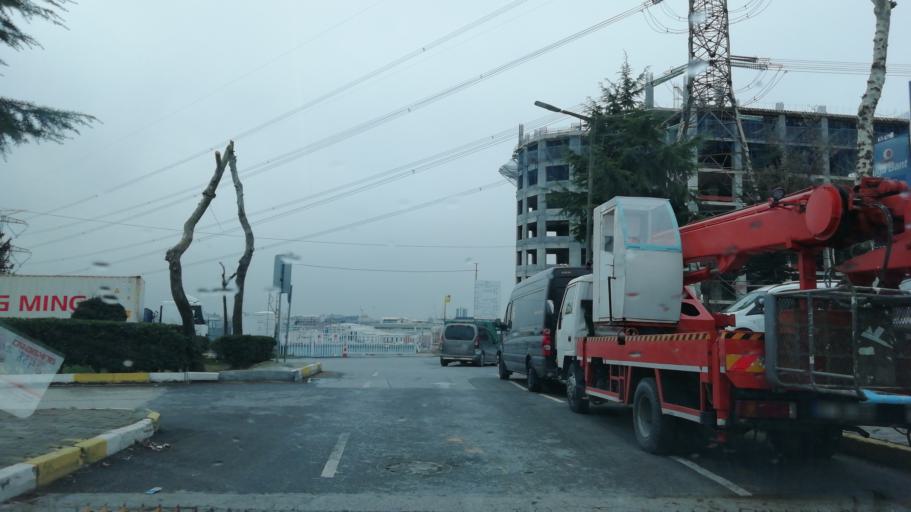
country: TR
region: Istanbul
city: Mahmutbey
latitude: 41.0674
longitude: 28.8189
